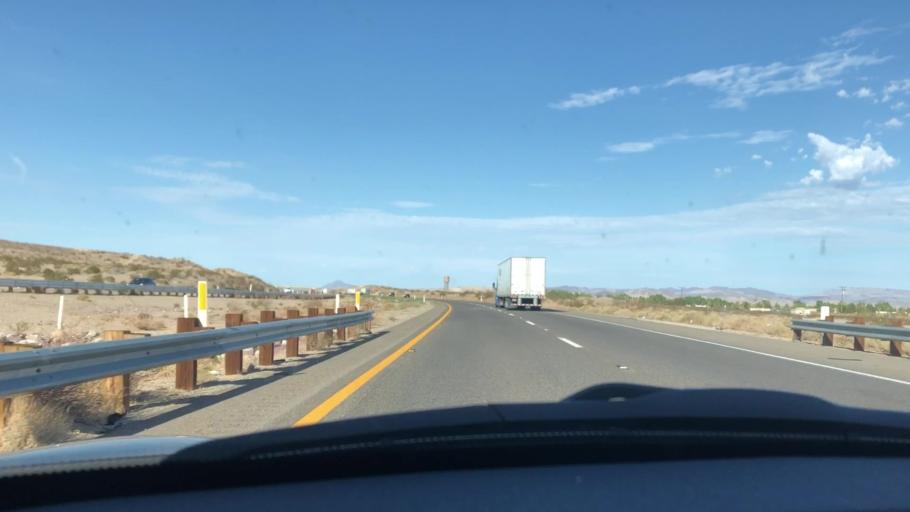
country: US
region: California
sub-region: San Bernardino County
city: Barstow
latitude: 34.9272
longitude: -116.7261
